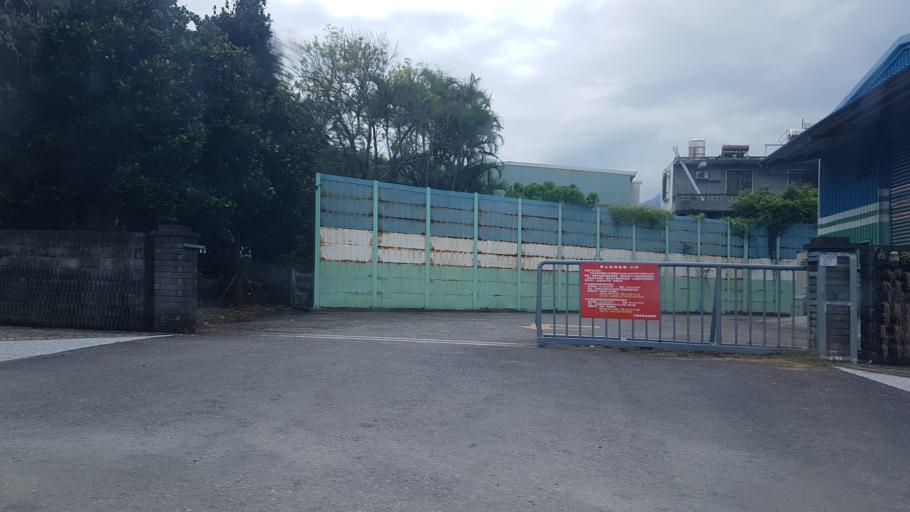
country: TW
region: Taiwan
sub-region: Hualien
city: Hualian
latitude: 23.9969
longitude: 121.6332
